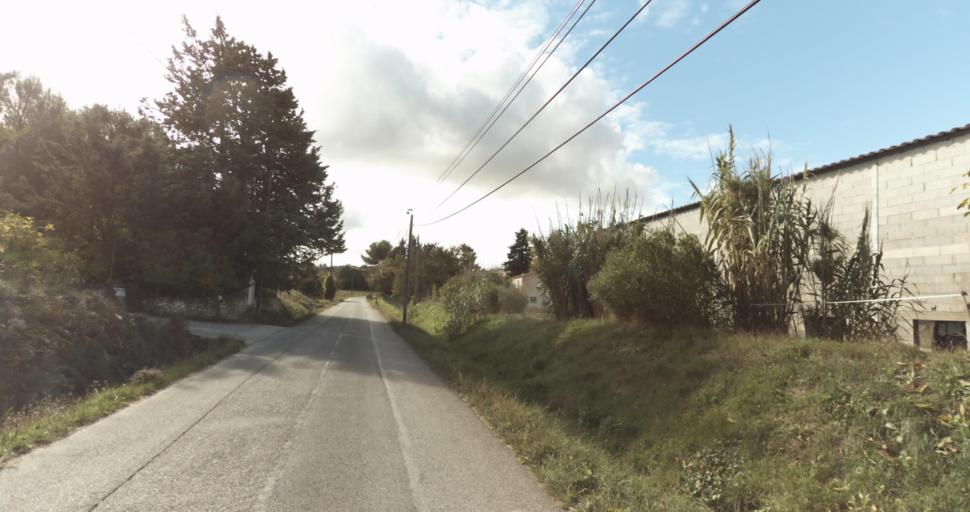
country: FR
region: Provence-Alpes-Cote d'Azur
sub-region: Departement des Bouches-du-Rhone
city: Venelles
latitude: 43.5813
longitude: 5.4993
